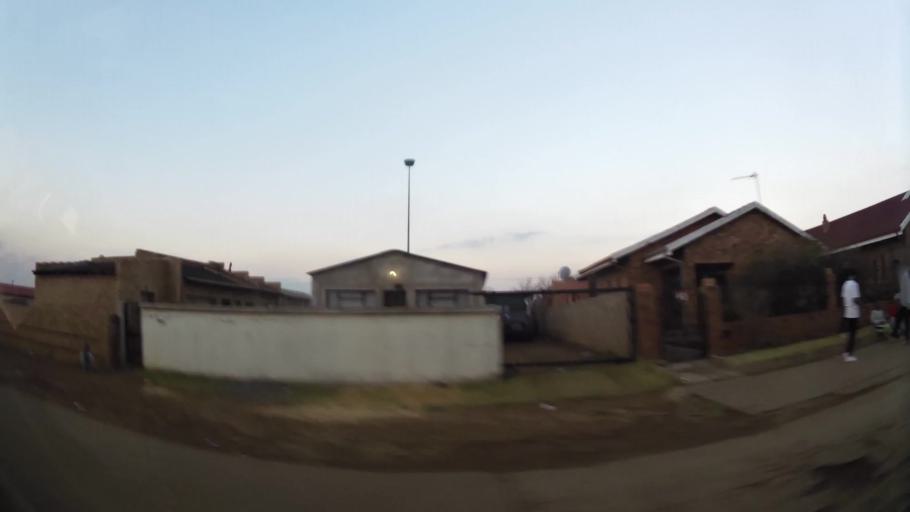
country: ZA
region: Gauteng
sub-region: City of Johannesburg Metropolitan Municipality
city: Orange Farm
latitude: -26.5516
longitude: 27.8598
